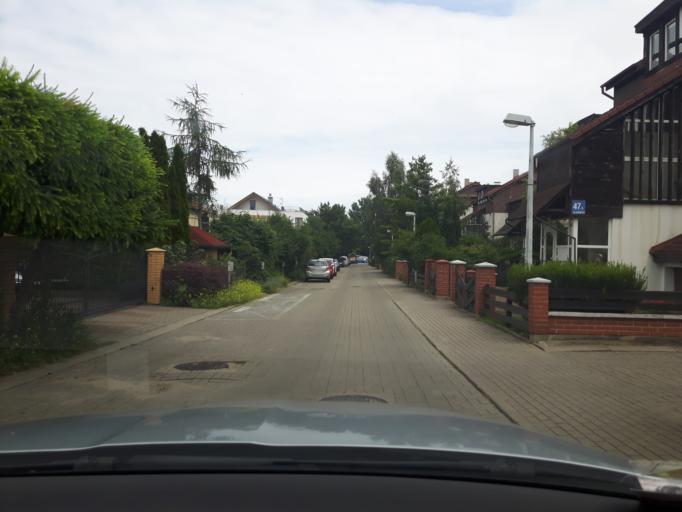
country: PL
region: Pomeranian Voivodeship
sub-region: Sopot
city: Sopot
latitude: 54.4309
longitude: 18.5740
